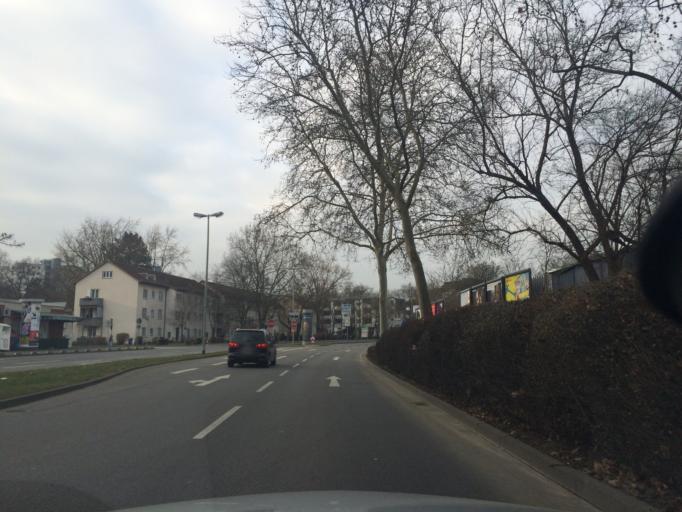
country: DE
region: Hesse
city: Niederrad
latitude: 50.1197
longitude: 8.6226
